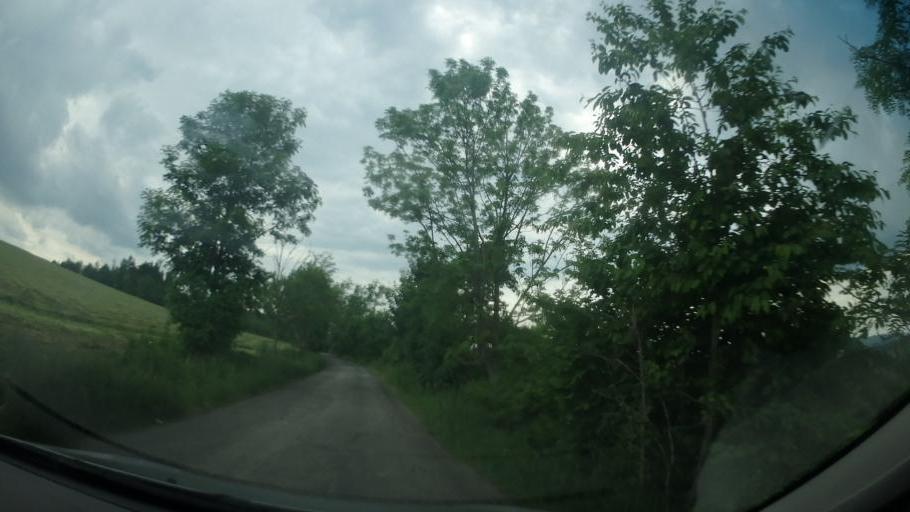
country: CZ
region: South Moravian
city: Olesnice
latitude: 49.4904
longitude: 16.4173
